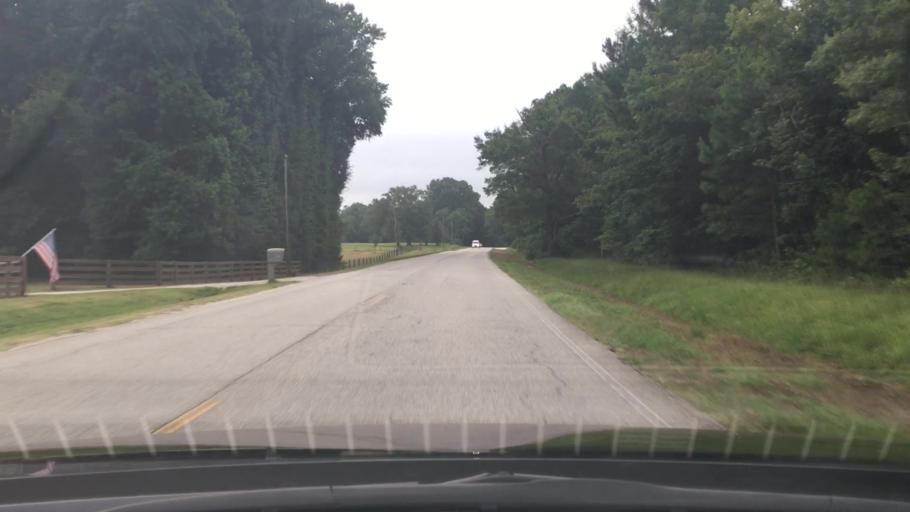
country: US
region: Georgia
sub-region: Coweta County
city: Senoia
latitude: 33.2851
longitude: -84.4314
